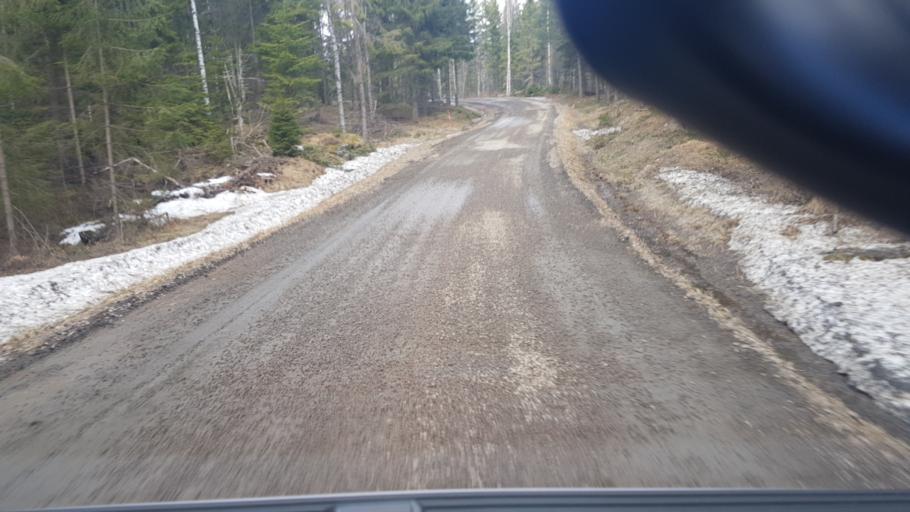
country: SE
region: Vaermland
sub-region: Eda Kommun
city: Amotfors
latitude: 59.7980
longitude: 12.4447
